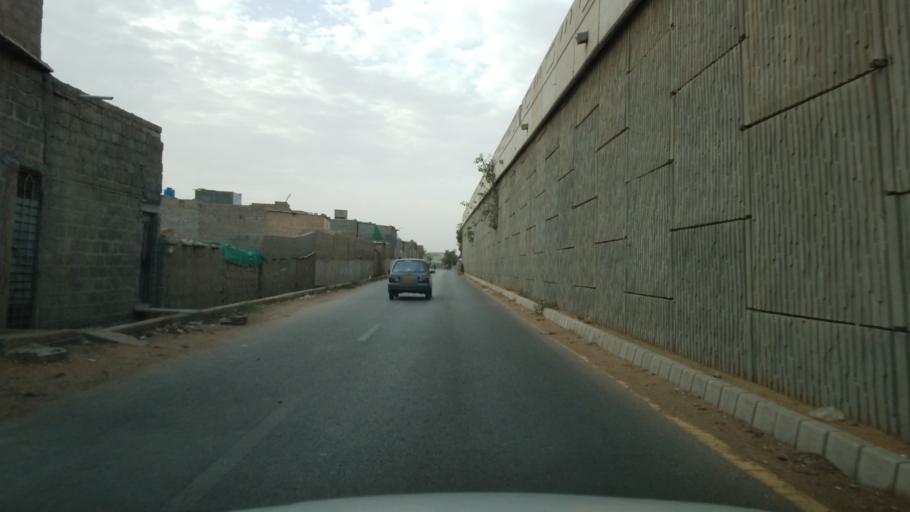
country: PK
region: Sindh
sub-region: Karachi District
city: Karachi
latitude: 24.9439
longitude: 67.0874
